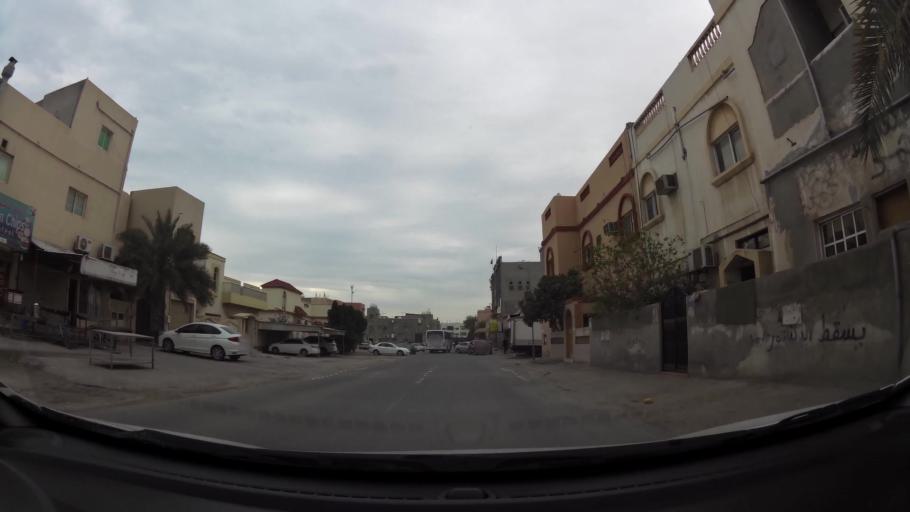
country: BH
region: Northern
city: Sitrah
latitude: 26.1673
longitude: 50.6077
